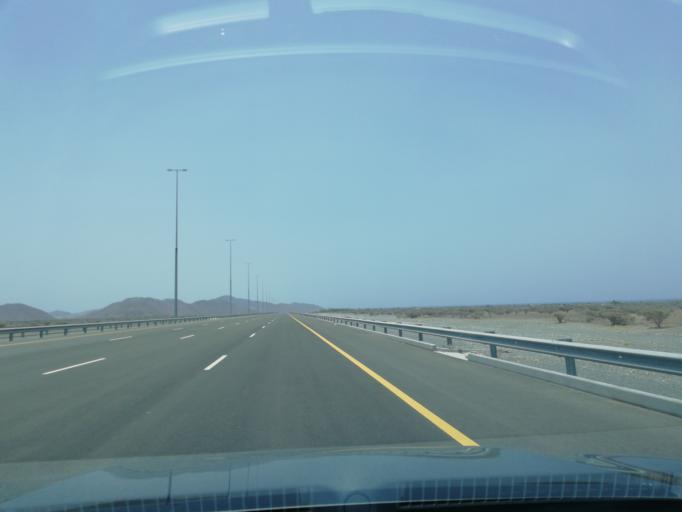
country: OM
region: Al Batinah
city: Shinas
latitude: 24.9135
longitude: 56.3550
